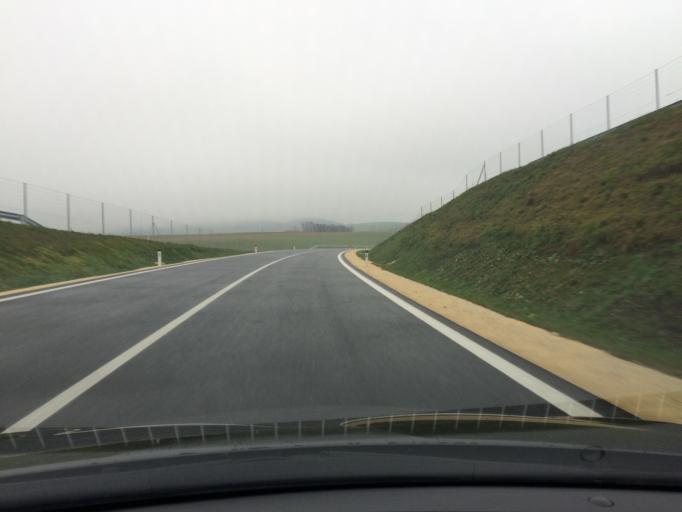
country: AT
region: Lower Austria
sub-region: Politischer Bezirk Mistelbach
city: Mistelbach
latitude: 48.5482
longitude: 16.5646
